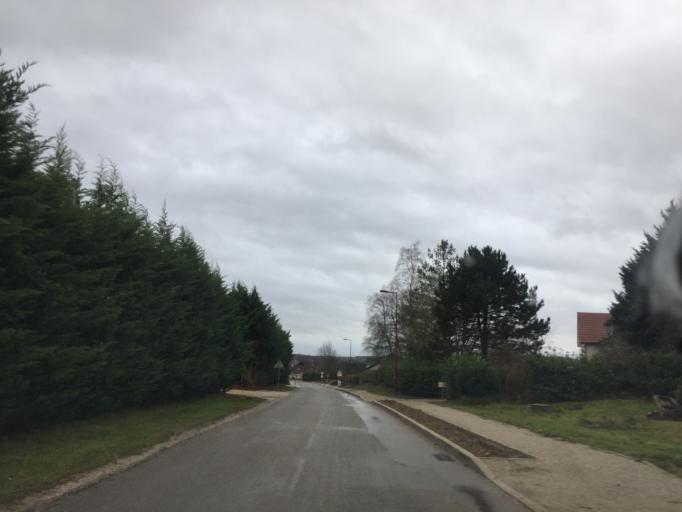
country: FR
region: Franche-Comte
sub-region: Departement du Jura
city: Orchamps
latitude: 47.1683
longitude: 5.5665
